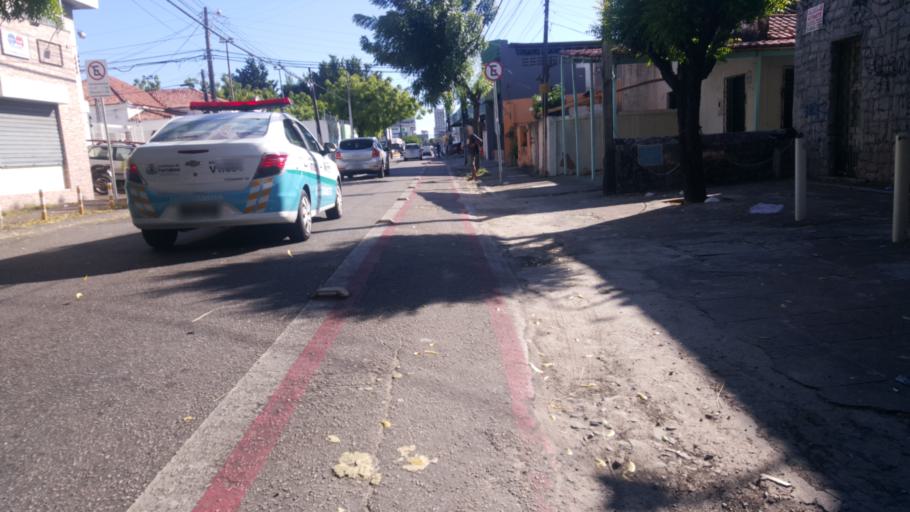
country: BR
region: Ceara
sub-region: Fortaleza
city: Fortaleza
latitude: -3.7411
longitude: -38.5329
